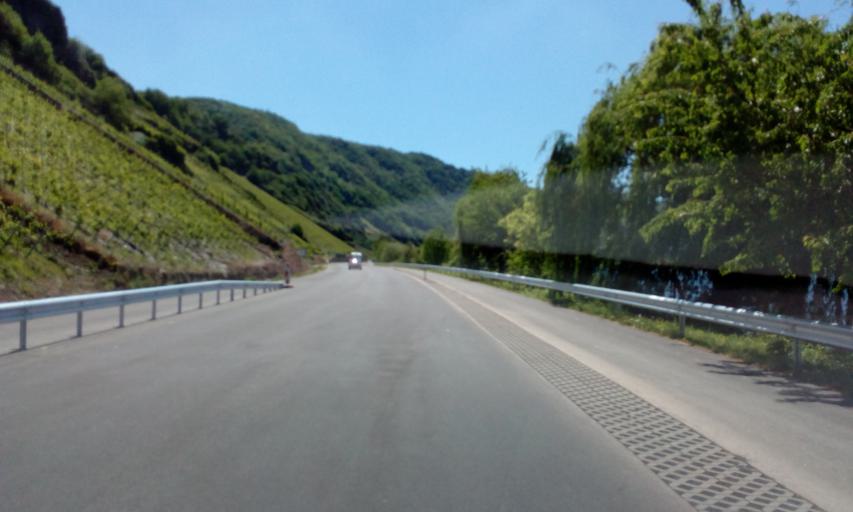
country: DE
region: Rheinland-Pfalz
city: Wintrich
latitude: 49.8741
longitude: 6.9494
